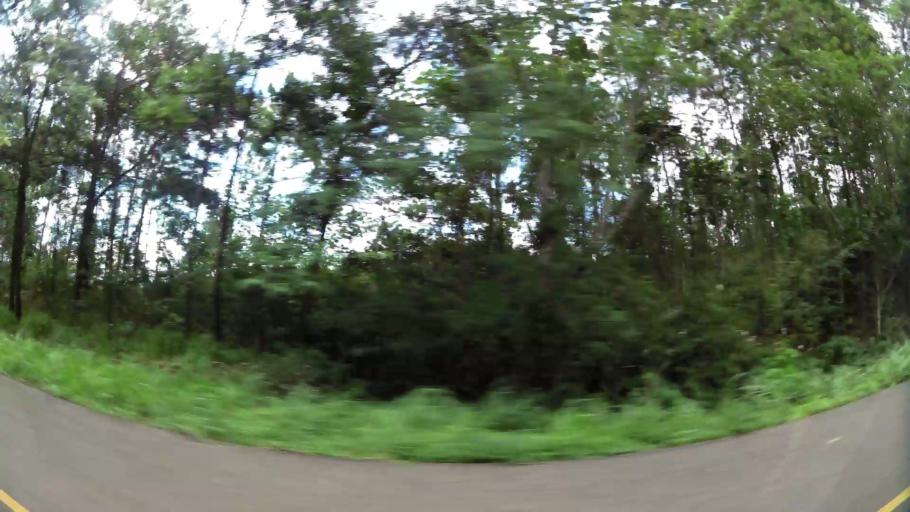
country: DO
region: La Vega
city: Rincon
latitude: 19.1138
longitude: -70.4462
